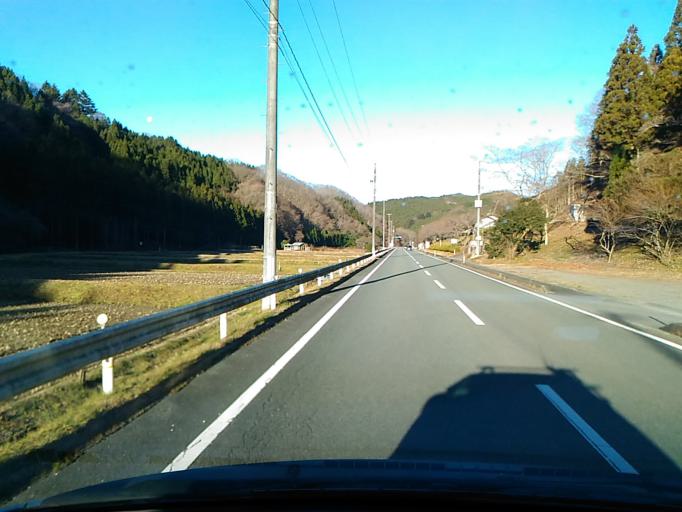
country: JP
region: Ibaraki
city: Kitaibaraki
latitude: 36.9400
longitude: 140.6636
